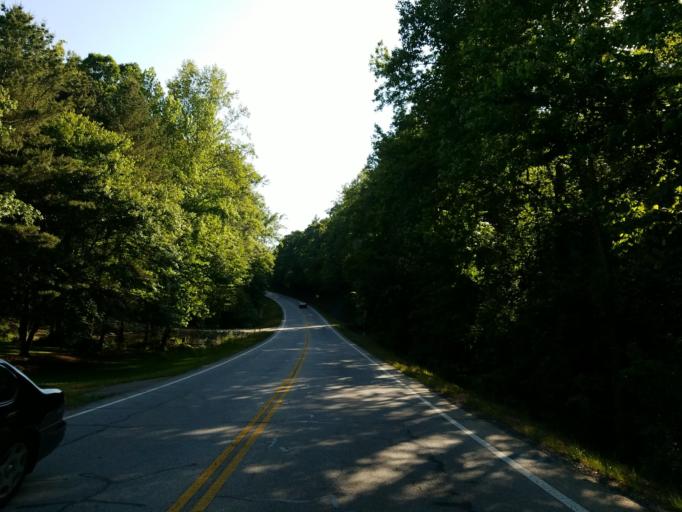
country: US
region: Georgia
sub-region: Paulding County
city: Dallas
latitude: 33.8588
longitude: -84.9236
